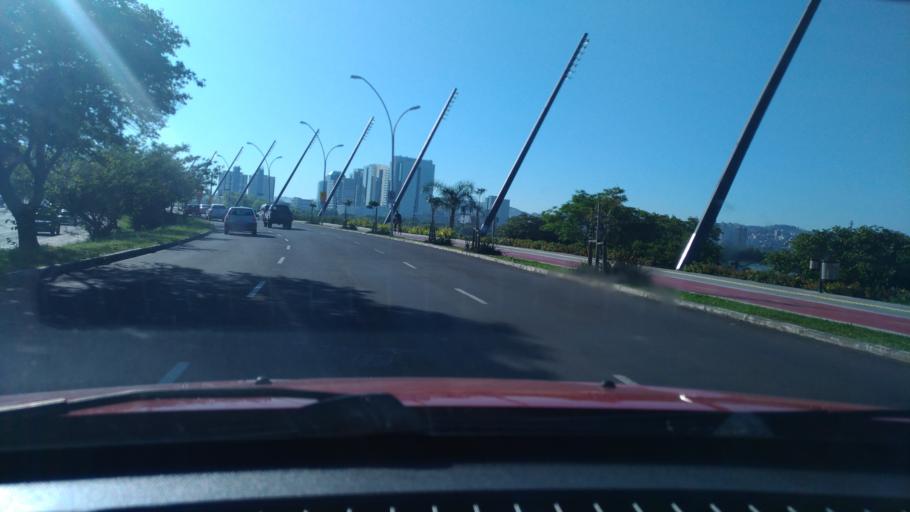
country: BR
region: Rio Grande do Sul
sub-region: Porto Alegre
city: Porto Alegre
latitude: -30.0420
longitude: -51.2398
